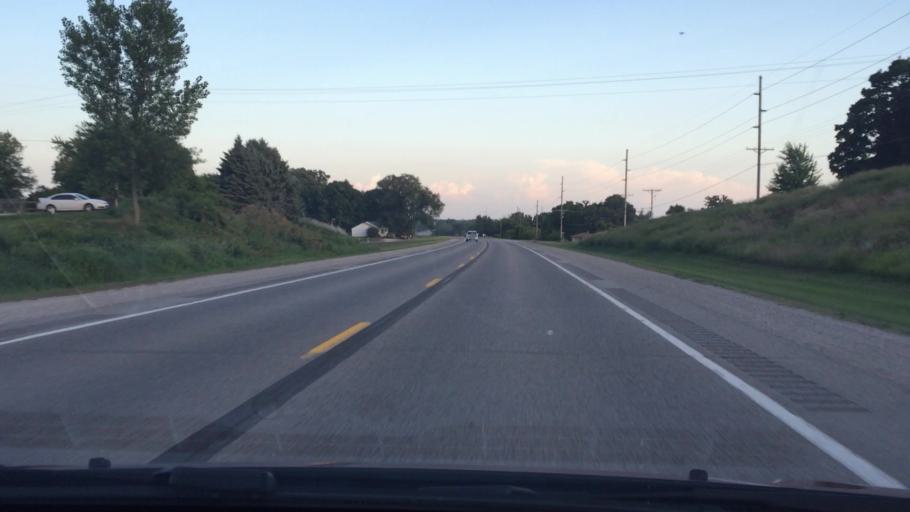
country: US
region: Iowa
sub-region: Muscatine County
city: Muscatine
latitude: 41.4721
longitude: -91.0373
